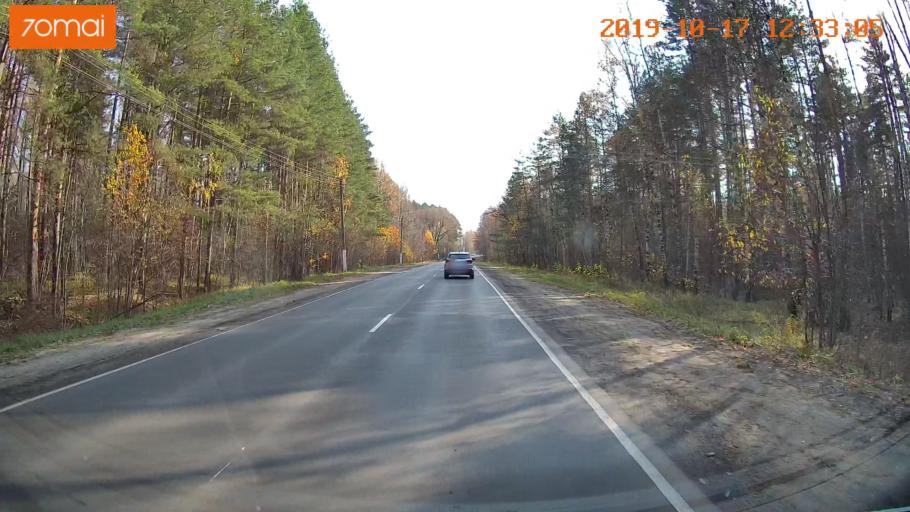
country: RU
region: Rjazan
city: Kasimov
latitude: 54.9576
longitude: 41.3500
